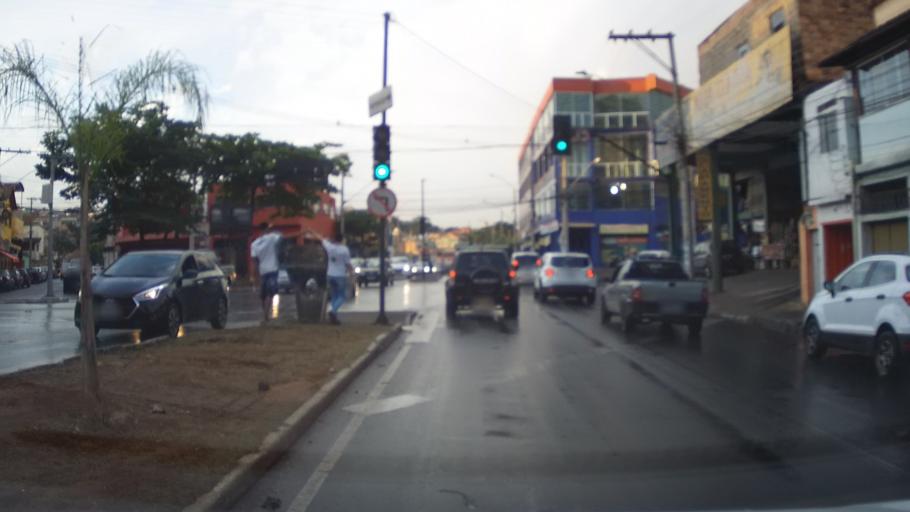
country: BR
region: Minas Gerais
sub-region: Belo Horizonte
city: Belo Horizonte
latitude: -19.9573
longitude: -43.9863
